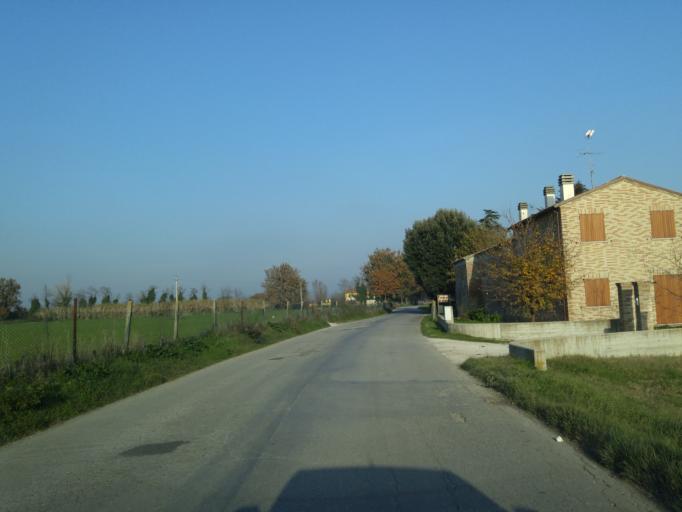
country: IT
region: The Marches
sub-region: Provincia di Pesaro e Urbino
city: Bellocchi
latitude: 43.7882
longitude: 12.9845
